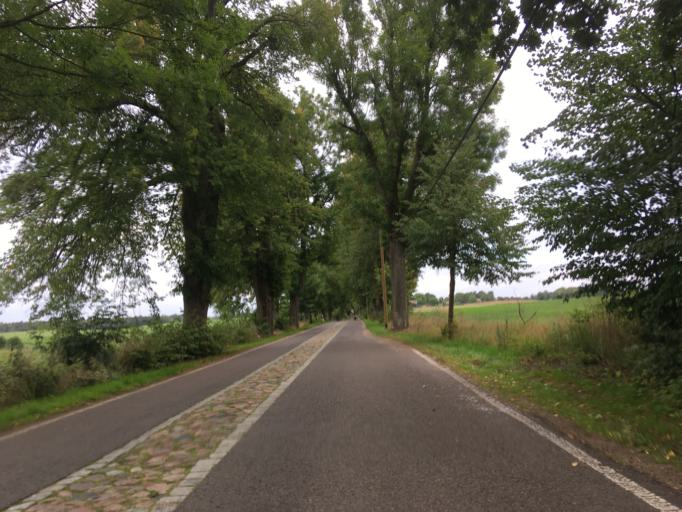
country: DE
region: Brandenburg
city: Joachimsthal
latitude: 53.0167
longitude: 13.7598
